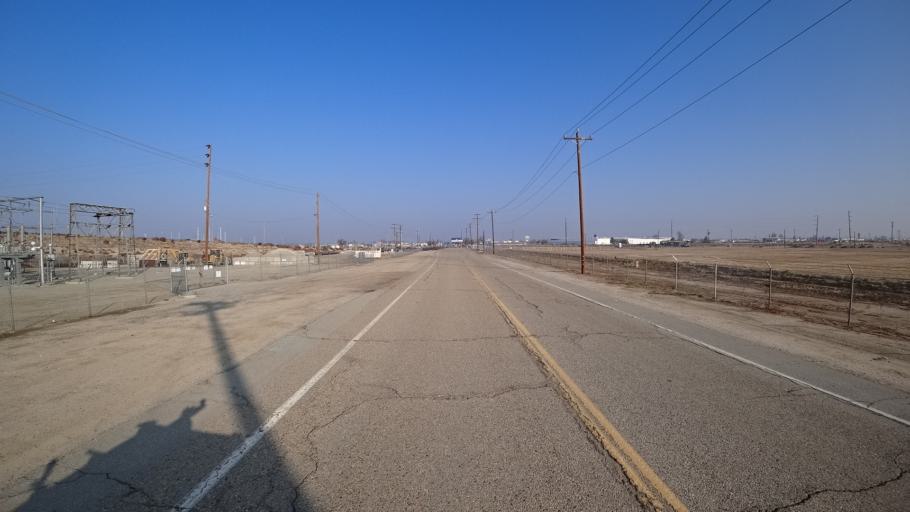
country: US
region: California
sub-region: Kern County
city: Greenacres
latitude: 35.3770
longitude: -119.0922
